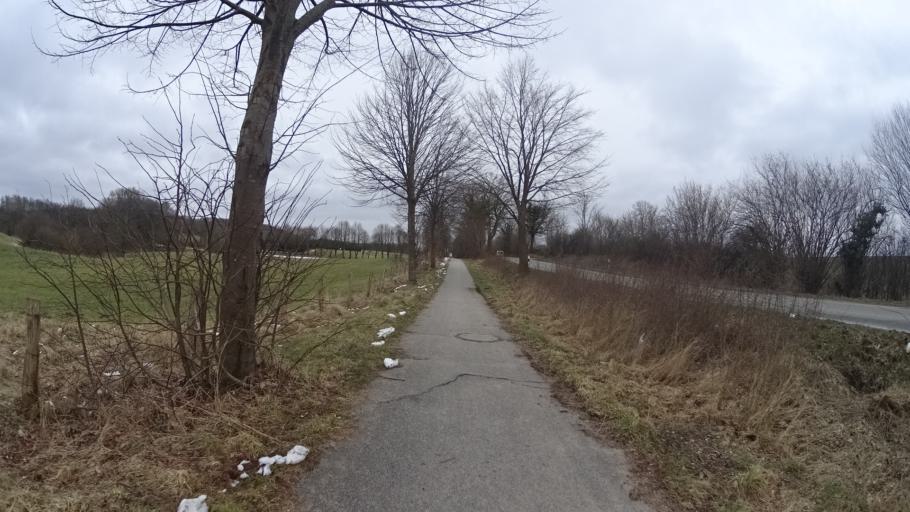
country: DE
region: Schleswig-Holstein
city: Neukirchen
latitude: 54.2002
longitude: 10.5610
